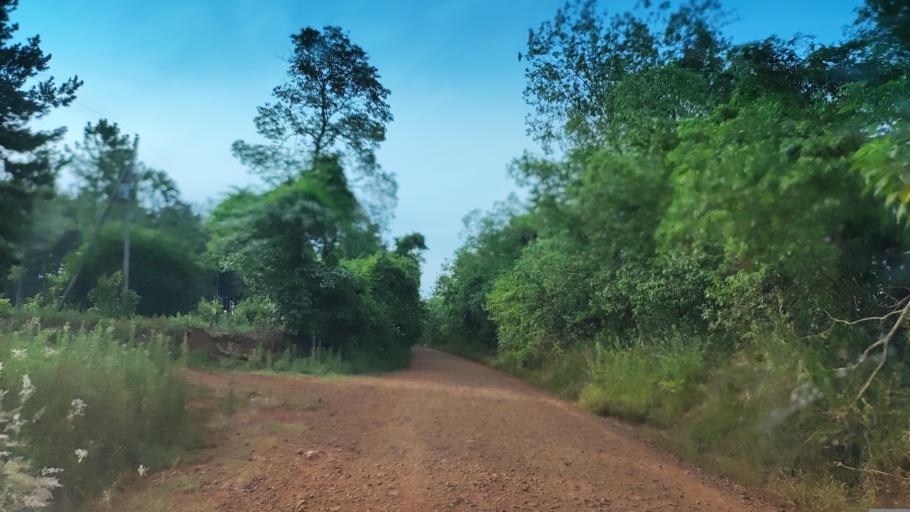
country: AR
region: Misiones
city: Gobernador Roca
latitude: -27.1710
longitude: -55.5080
